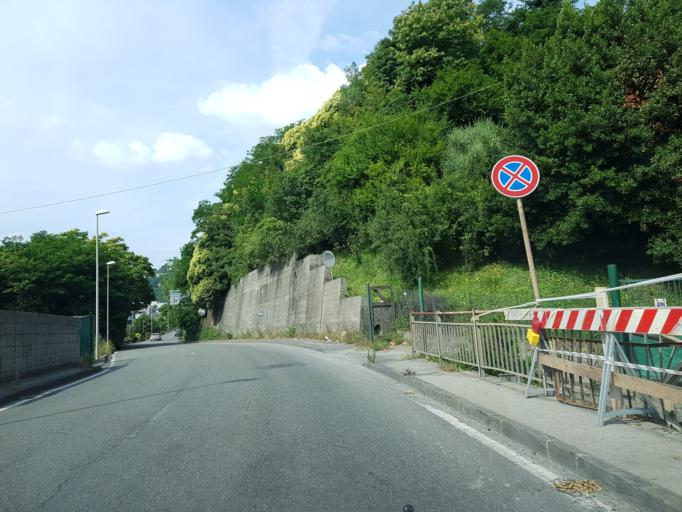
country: IT
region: Liguria
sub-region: Provincia di Genova
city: Manesseno
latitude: 44.4734
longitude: 8.9079
